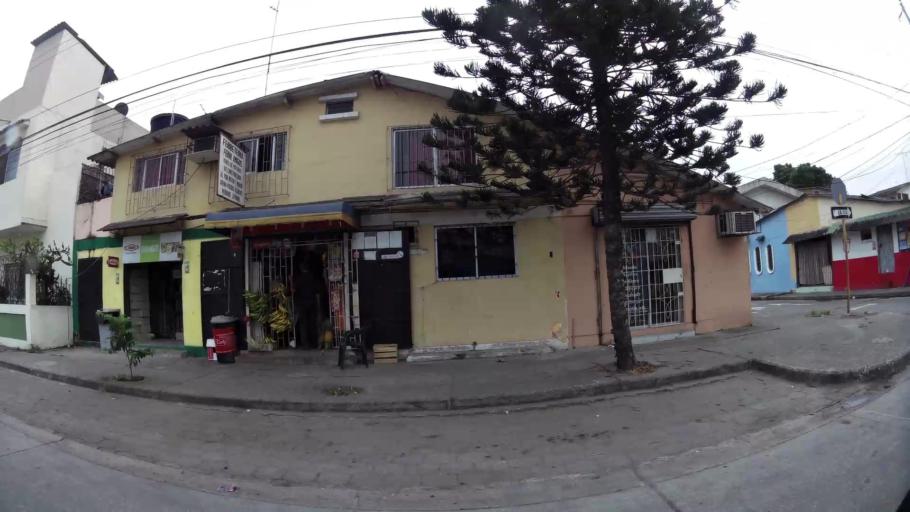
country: EC
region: Guayas
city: Eloy Alfaro
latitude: -2.1393
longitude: -79.9026
